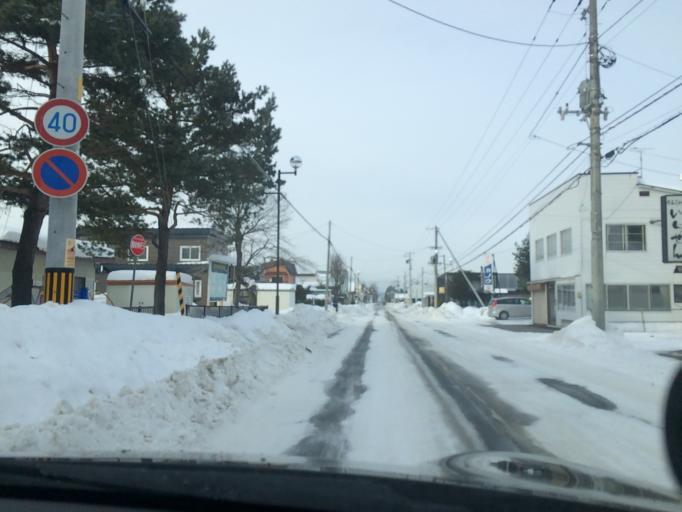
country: JP
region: Hokkaido
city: Obihiro
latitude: 42.9133
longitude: 143.0495
